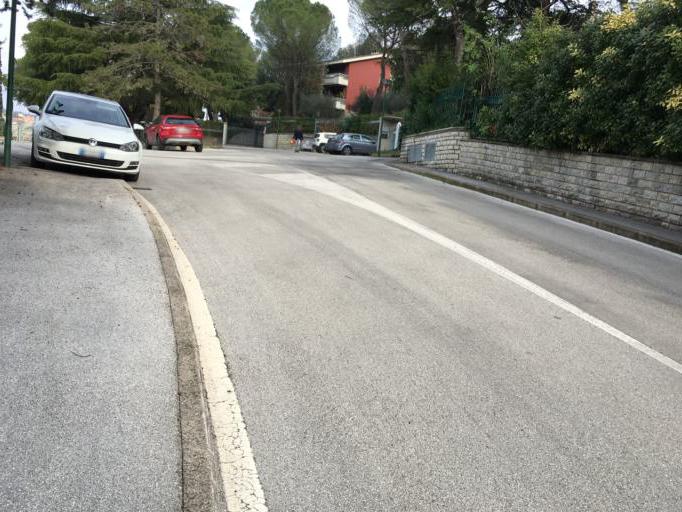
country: IT
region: Umbria
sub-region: Provincia di Perugia
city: Perugia
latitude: 43.0968
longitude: 12.3722
